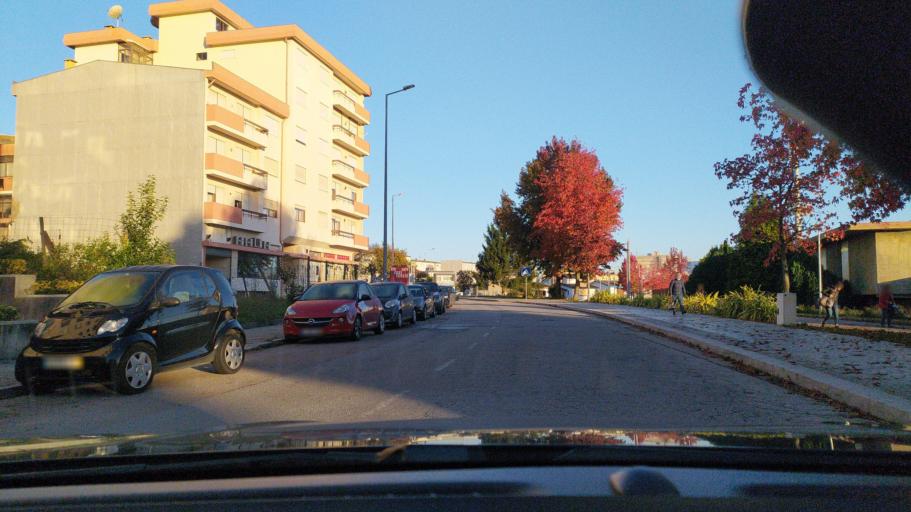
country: PT
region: Porto
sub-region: Maia
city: Maia
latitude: 41.2335
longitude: -8.6188
